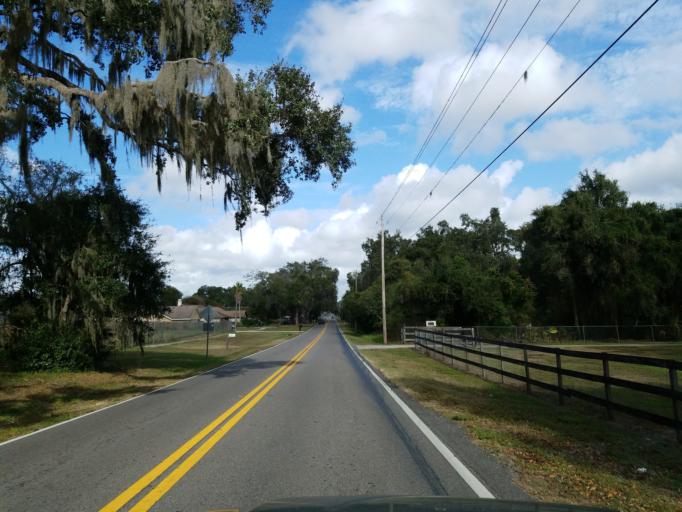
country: US
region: Florida
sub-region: Hillsborough County
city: Bloomingdale
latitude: 27.9097
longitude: -82.2195
